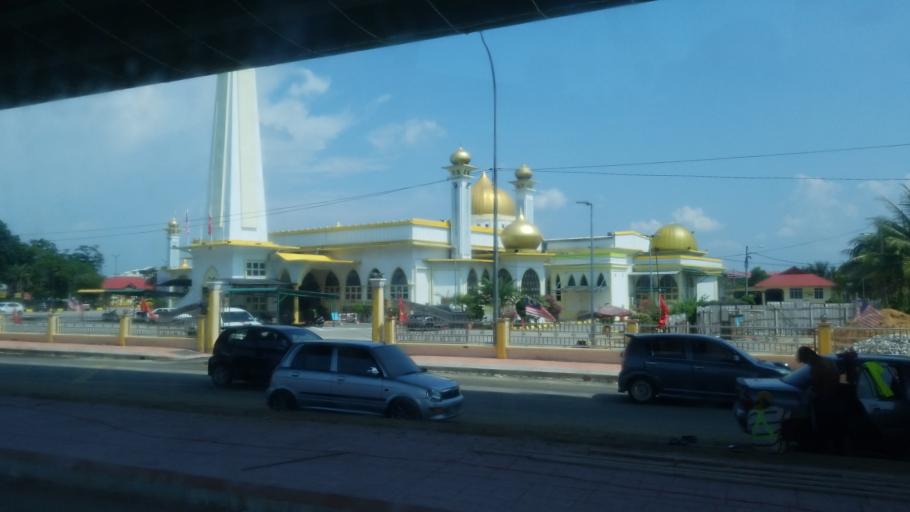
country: MY
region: Kelantan
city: Tanah Merah
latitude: 5.8091
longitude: 102.1453
